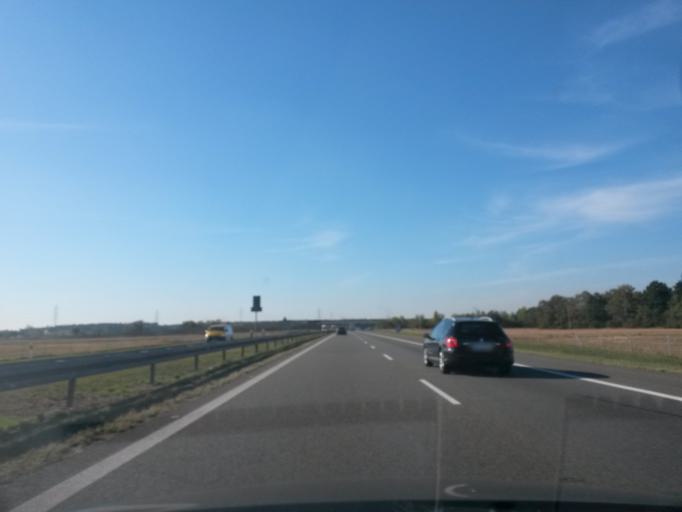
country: PL
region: Opole Voivodeship
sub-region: Powiat krapkowicki
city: Krapkowice
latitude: 50.5262
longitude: 17.9269
